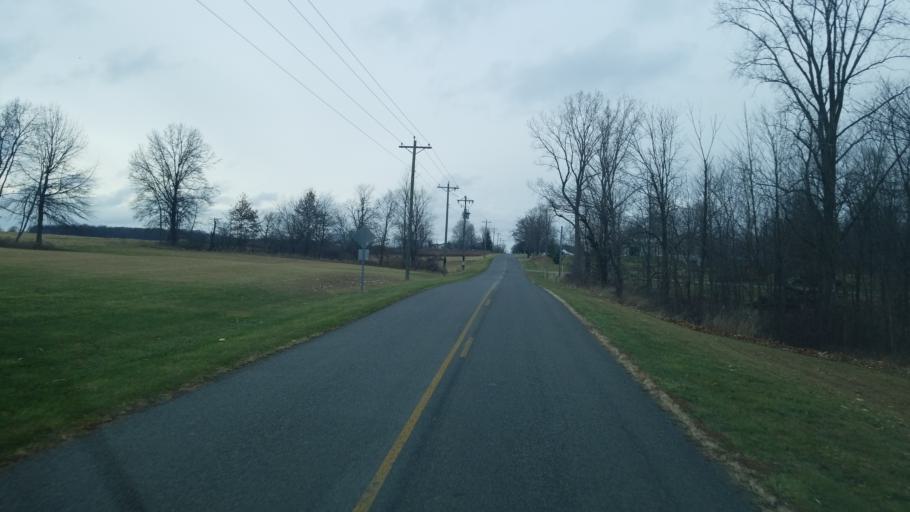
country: US
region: Ohio
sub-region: Union County
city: Marysville
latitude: 40.2832
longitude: -83.2716
